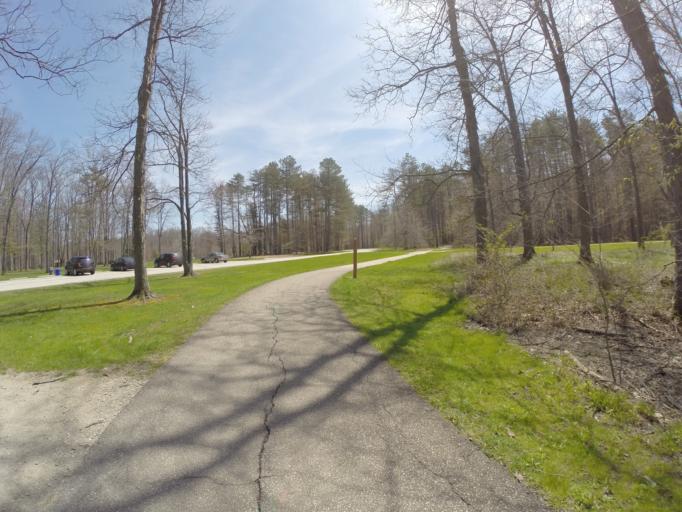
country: US
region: Ohio
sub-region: Cuyahoga County
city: Mayfield
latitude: 41.5616
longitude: -81.4325
